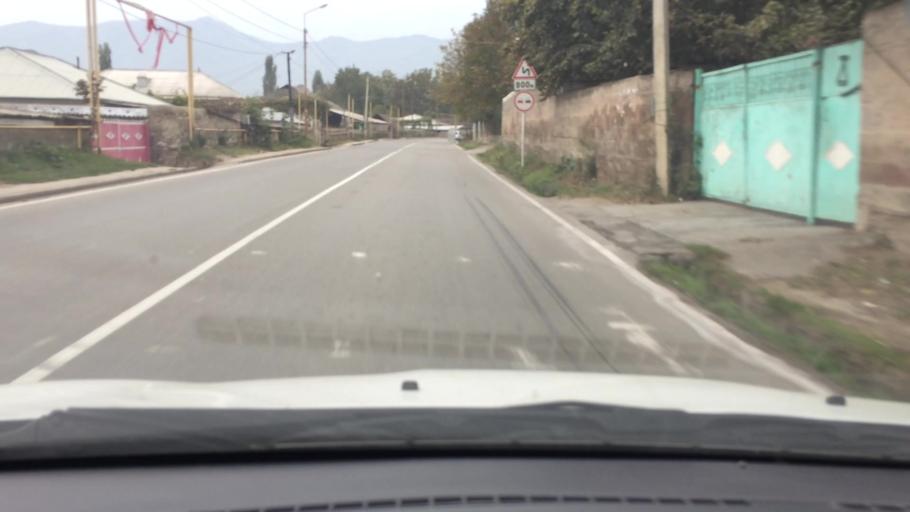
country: AM
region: Tavush
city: Bagratashen
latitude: 41.2498
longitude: 44.7999
